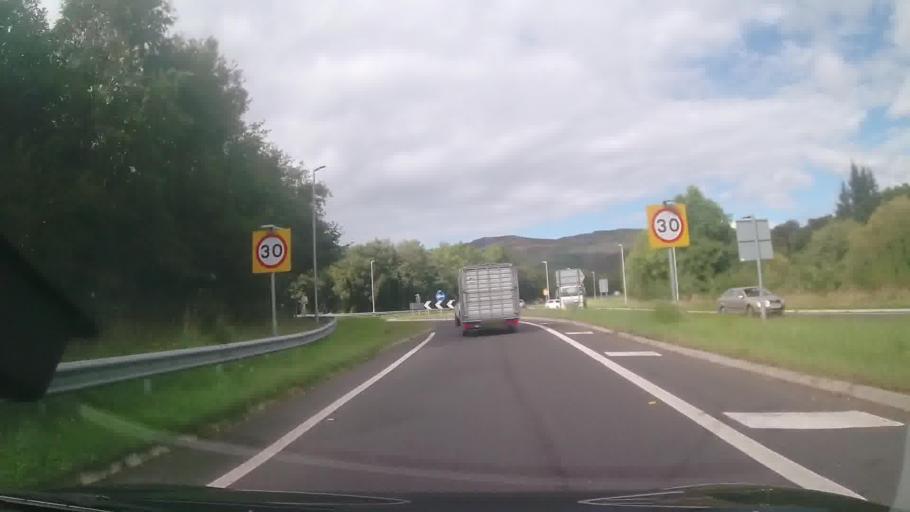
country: GB
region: Wales
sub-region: Gwynedd
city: Dolgellau
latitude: 52.7462
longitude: -3.9035
